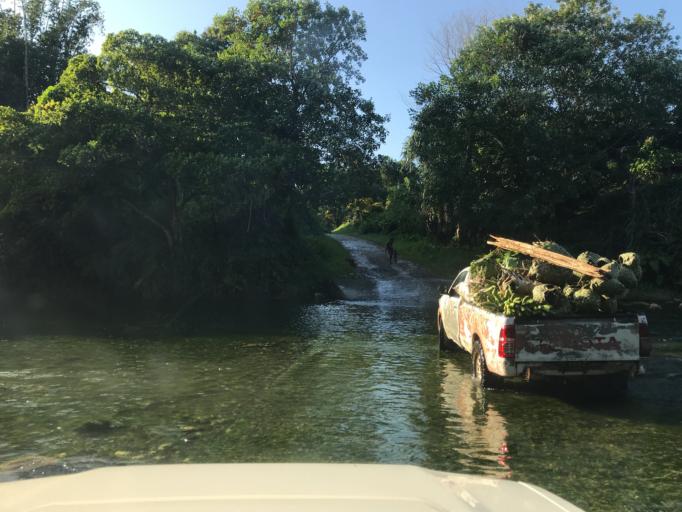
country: VU
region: Sanma
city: Luganville
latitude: -15.5950
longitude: 166.9003
